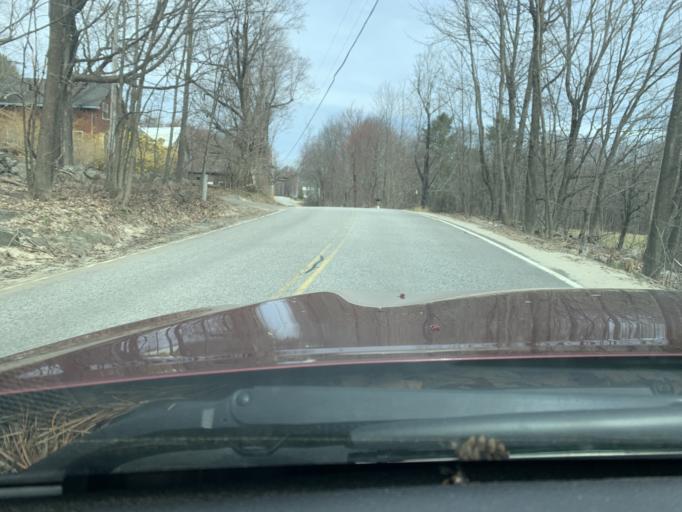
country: US
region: Maine
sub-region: Cumberland County
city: Raymond
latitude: 43.9534
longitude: -70.3864
